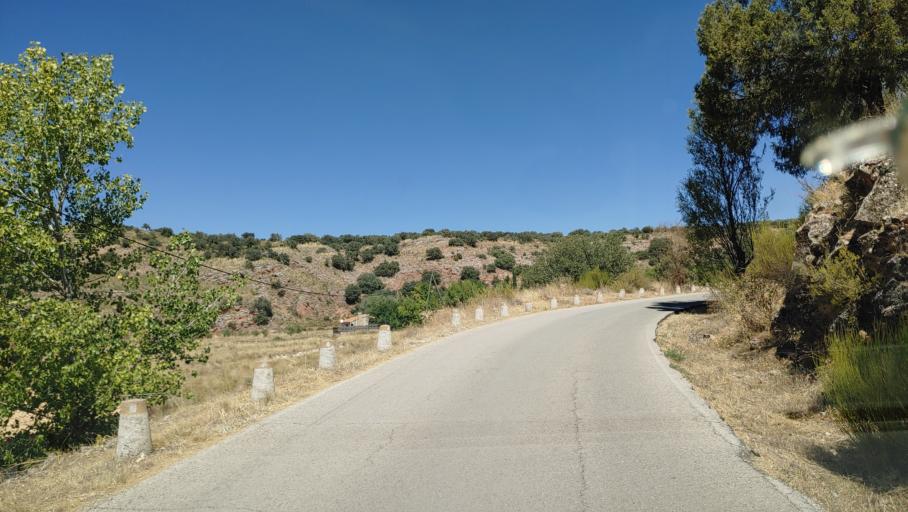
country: ES
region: Castille-La Mancha
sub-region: Provincia de Ciudad Real
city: Ruidera
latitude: 38.9257
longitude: -2.8325
